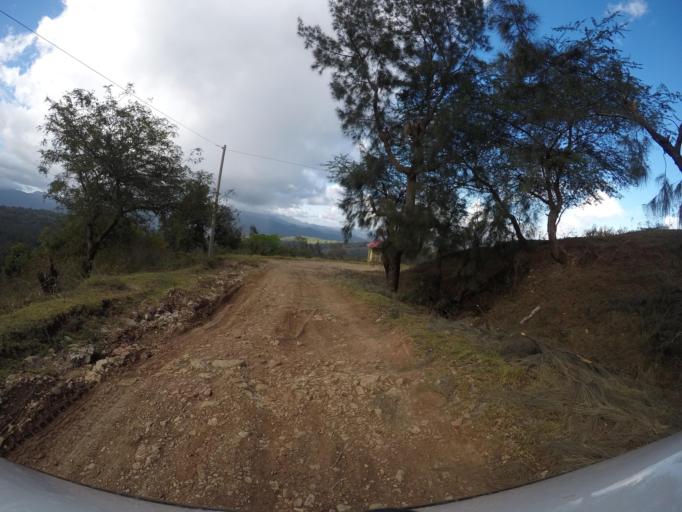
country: TL
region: Baucau
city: Venilale
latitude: -8.6867
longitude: 126.6636
